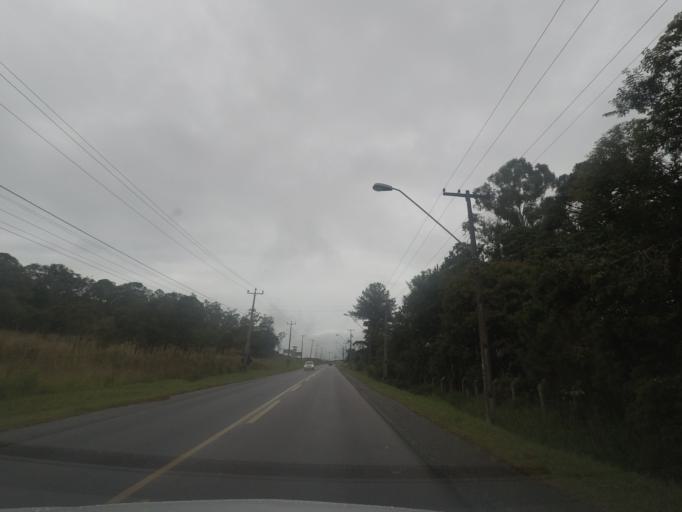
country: BR
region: Parana
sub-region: Campina Grande Do Sul
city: Campina Grande do Sul
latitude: -25.3252
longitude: -49.0785
